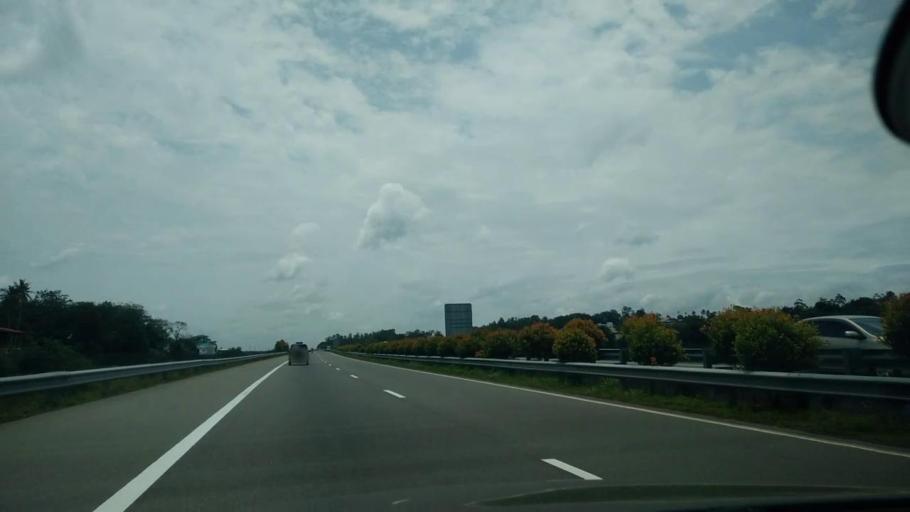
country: LK
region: Western
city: Homagama
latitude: 6.8897
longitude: 79.9771
